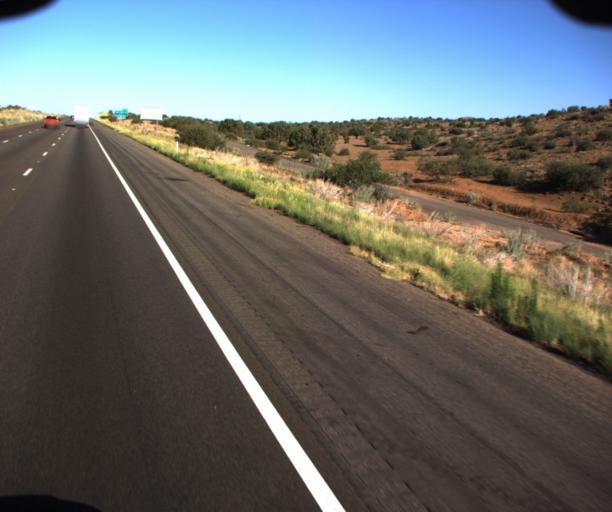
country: US
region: Arizona
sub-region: Mohave County
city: New Kingman-Butler
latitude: 35.1705
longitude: -113.7688
